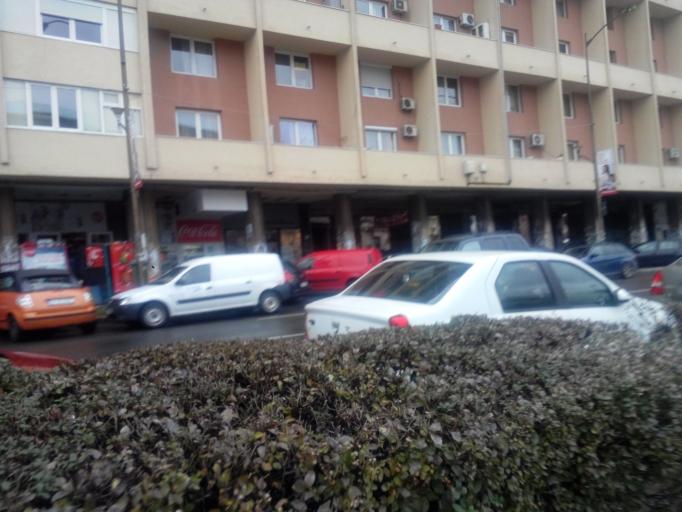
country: RO
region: Bucuresti
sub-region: Municipiul Bucuresti
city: Bucuresti
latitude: 44.4386
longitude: 26.0942
